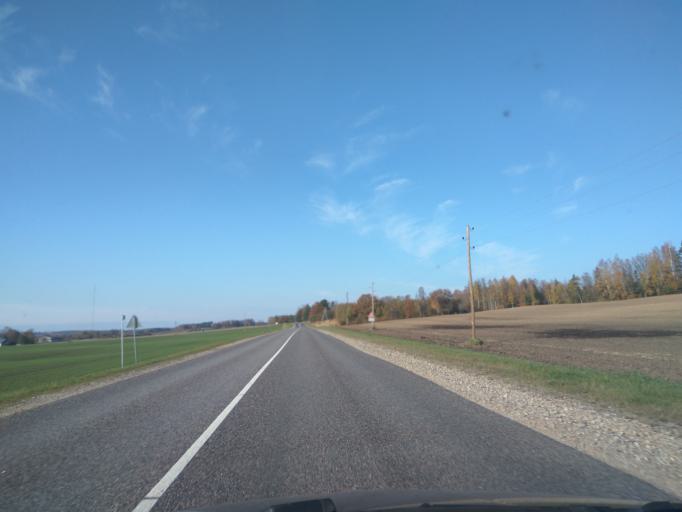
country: LV
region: Kuldigas Rajons
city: Kuldiga
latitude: 57.0235
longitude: 21.8640
